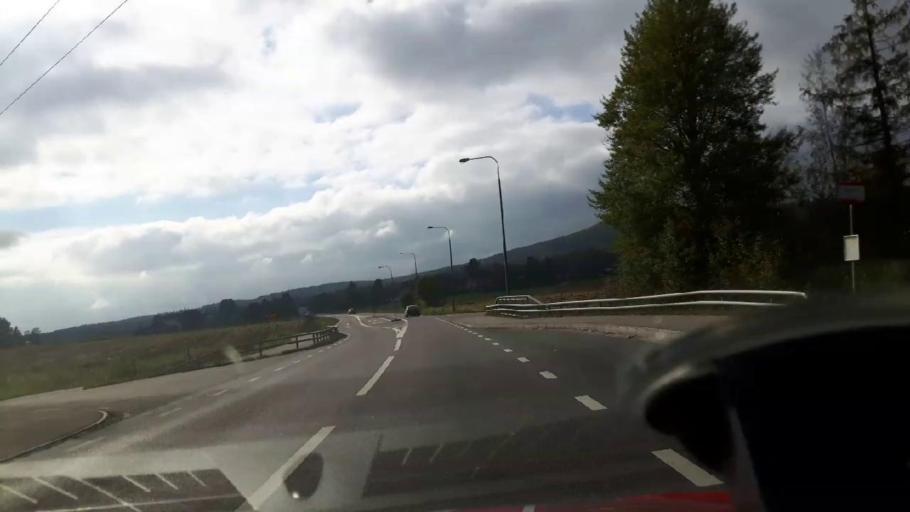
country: SE
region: Gaevleborg
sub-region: Bollnas Kommun
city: Arbra
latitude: 61.5133
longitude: 16.3604
